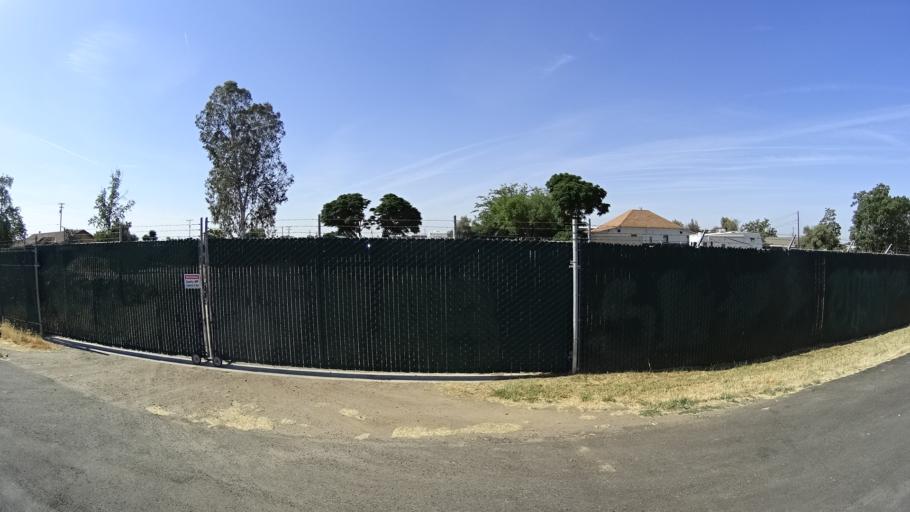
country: US
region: California
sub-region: Kings County
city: Hanford
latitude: 36.3313
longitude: -119.6338
